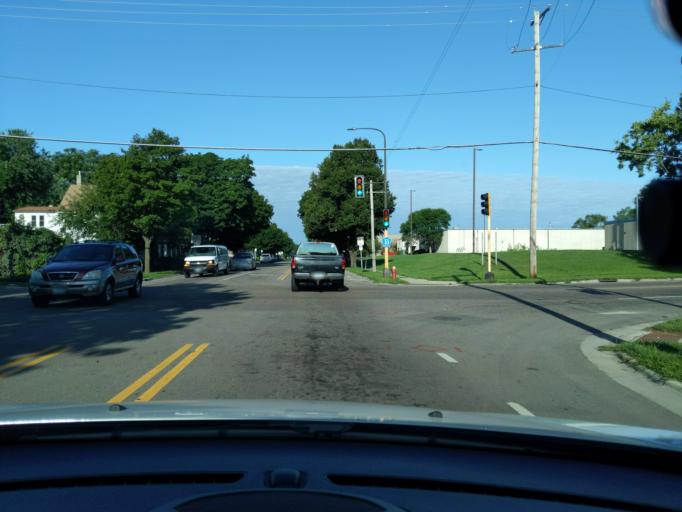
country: US
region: Minnesota
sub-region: Ramsey County
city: Saint Paul
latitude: 44.9630
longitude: -93.1159
